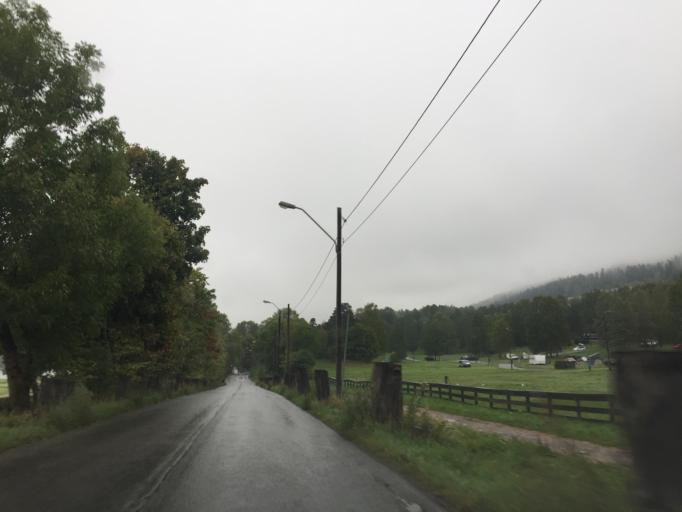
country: NO
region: Akershus
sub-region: Baerum
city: Lysaker
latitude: 59.9627
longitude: 10.6401
